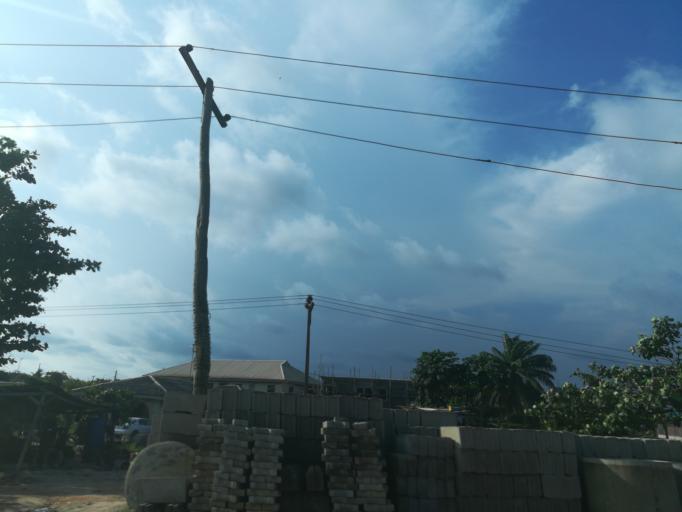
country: NG
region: Ogun
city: Ado Odo
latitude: 6.4950
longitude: 3.0839
